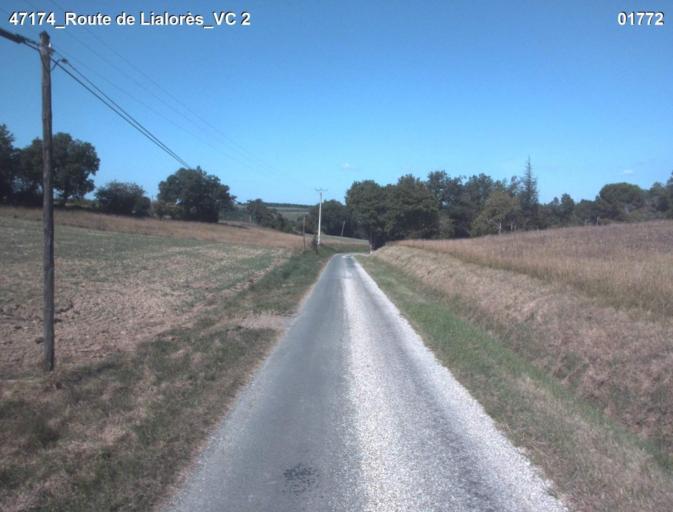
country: FR
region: Midi-Pyrenees
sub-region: Departement du Gers
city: Condom
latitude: 44.0207
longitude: 0.3728
